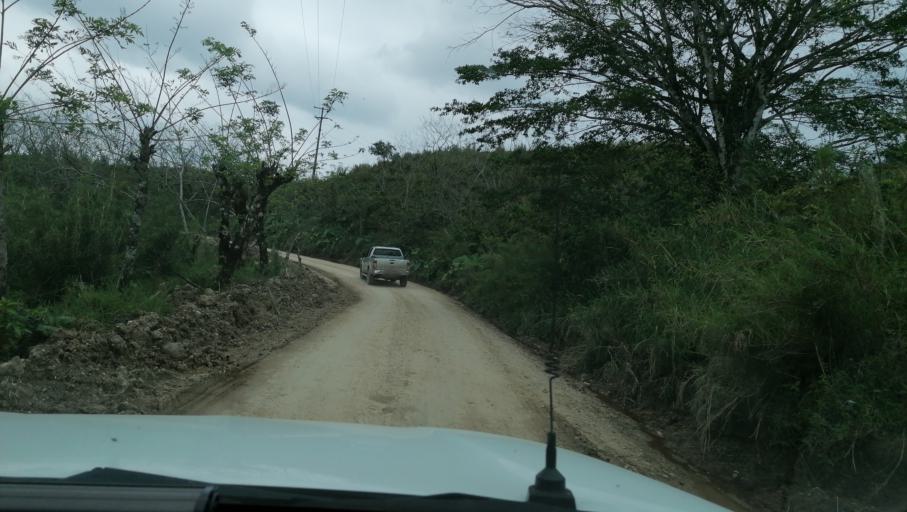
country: MX
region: Chiapas
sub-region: Ocotepec
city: San Pablo Huacano
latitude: 17.2690
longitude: -93.2578
